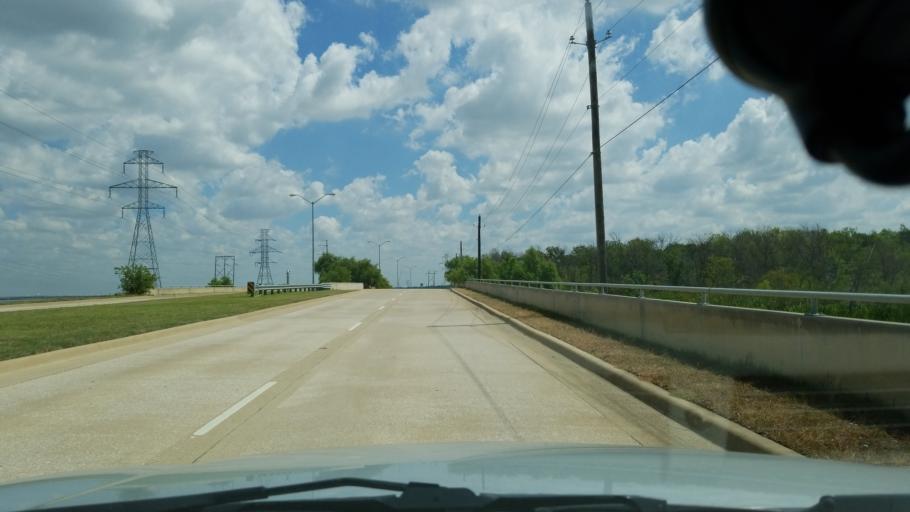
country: US
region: Texas
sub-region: Dallas County
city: Grand Prairie
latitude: 32.7153
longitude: -96.9504
